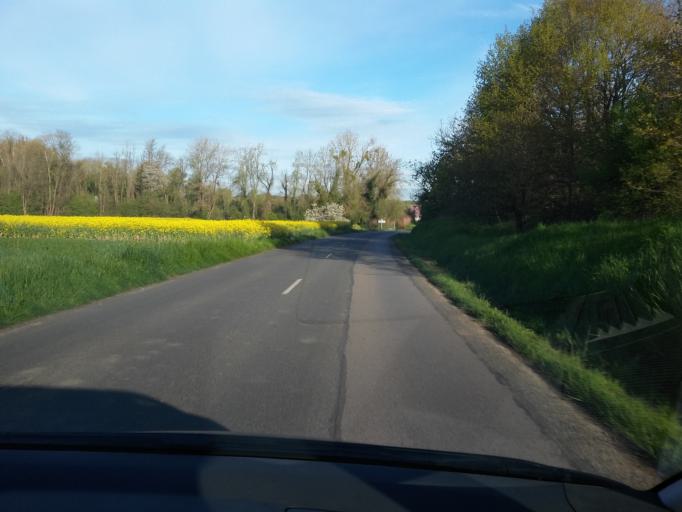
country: FR
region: Picardie
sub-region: Departement de l'Oise
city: Longueil-Sainte-Marie
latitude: 49.3489
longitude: 2.7248
